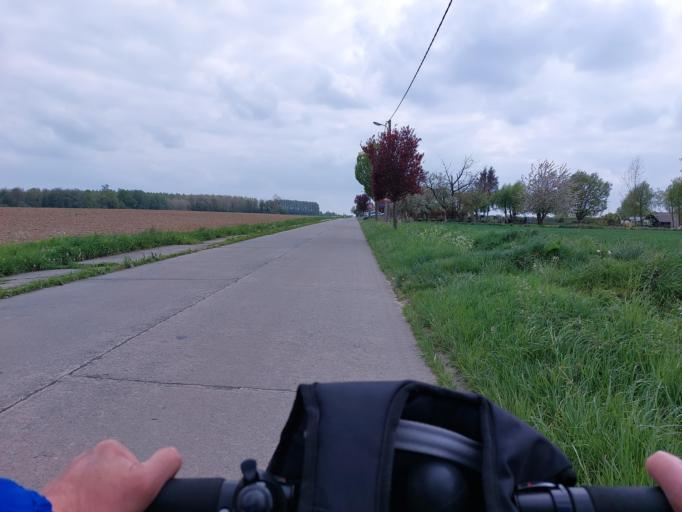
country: BE
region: Wallonia
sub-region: Province du Hainaut
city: Dour
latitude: 50.3617
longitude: 3.7345
